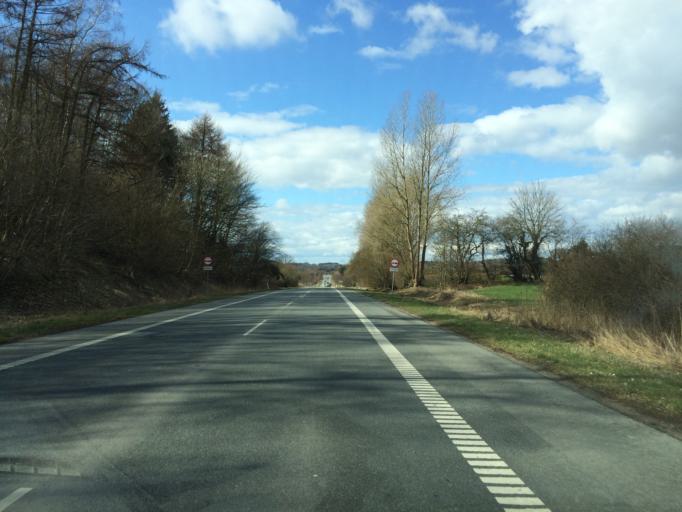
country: DK
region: South Denmark
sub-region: Assens Kommune
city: Vissenbjerg
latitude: 55.3950
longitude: 10.1055
